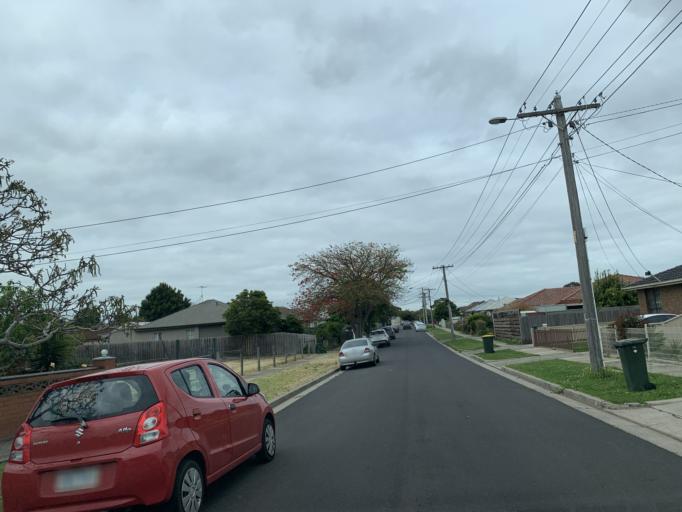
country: AU
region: Victoria
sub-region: Brimbank
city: St Albans
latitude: -37.7448
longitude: 144.7905
